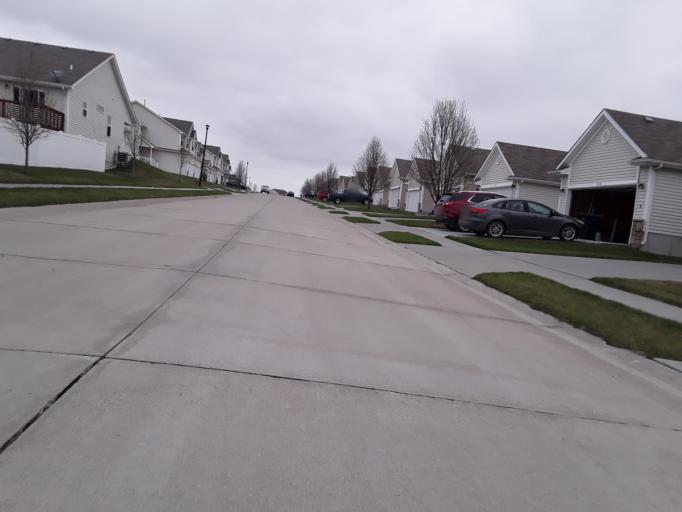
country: US
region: Nebraska
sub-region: Lancaster County
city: Lincoln
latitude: 40.8432
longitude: -96.5996
